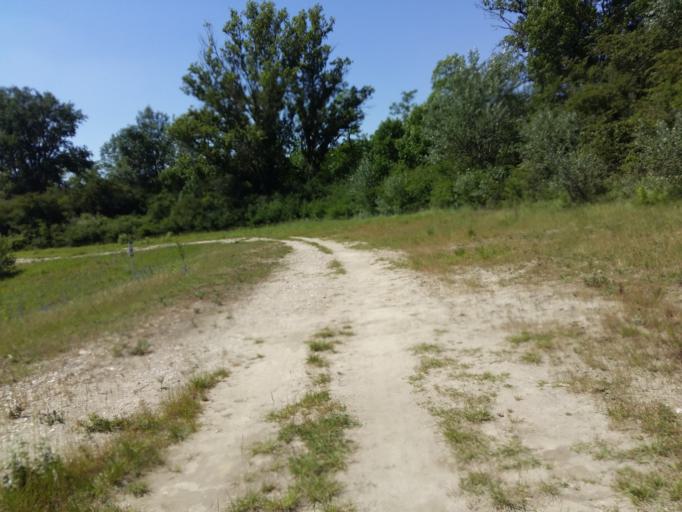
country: FR
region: Rhone-Alpes
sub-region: Departement de l'Ain
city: Saint-Maurice-de-Beynost
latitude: 45.8153
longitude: 4.9717
